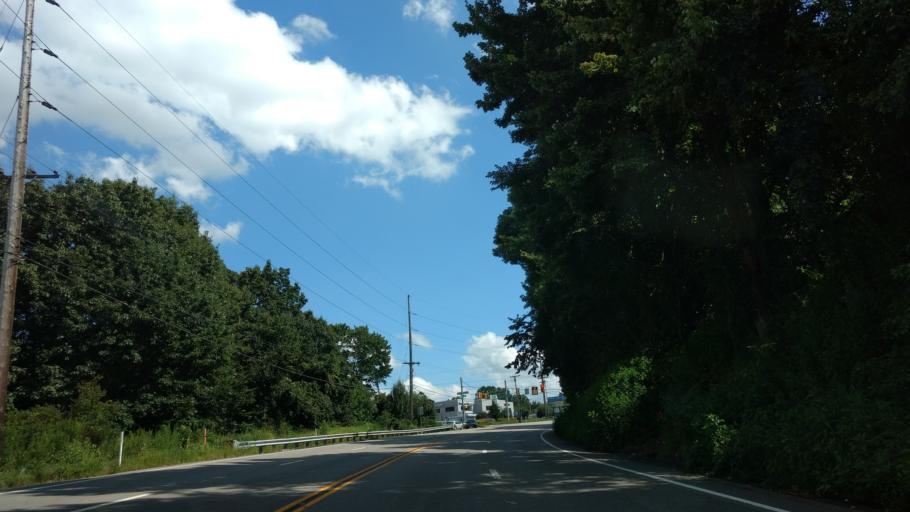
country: US
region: Pennsylvania
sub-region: Allegheny County
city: Franklin Park
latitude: 40.5830
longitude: -80.0388
